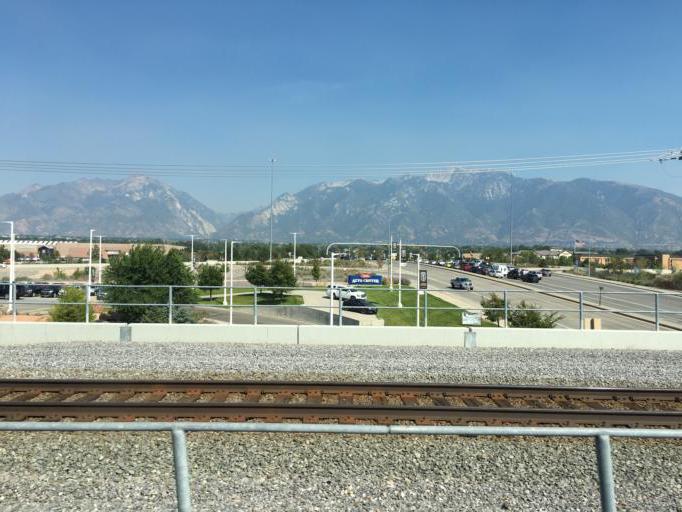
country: US
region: Utah
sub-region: Salt Lake County
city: South Jordan
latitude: 40.5594
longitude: -111.9012
